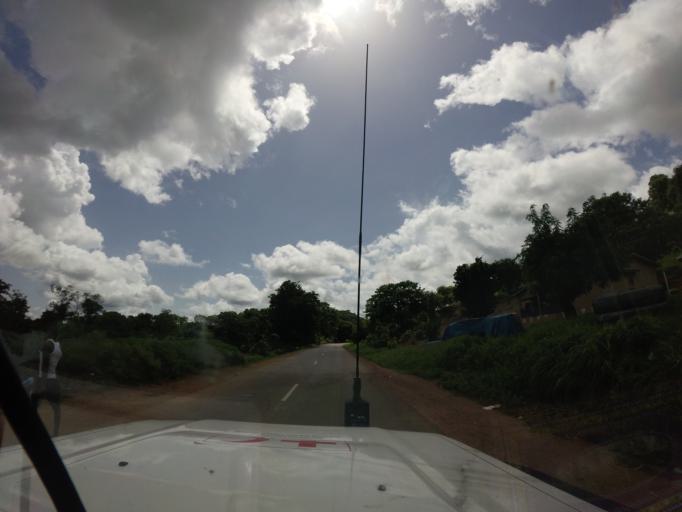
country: SL
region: Northern Province
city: Bindi
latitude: 10.1413
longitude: -11.6675
